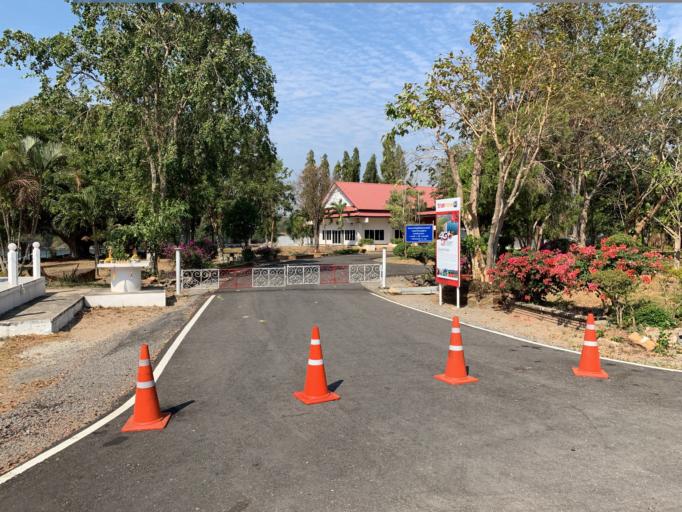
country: TH
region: Nakhon Ratchasima
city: Amphoe Sikhiu
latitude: 14.8640
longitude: 101.5628
